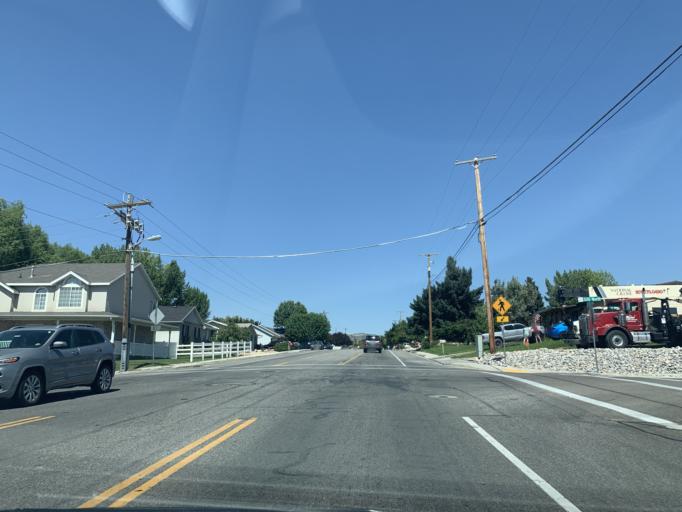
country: US
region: Utah
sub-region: Utah County
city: Lehi
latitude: 40.3940
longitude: -111.8301
